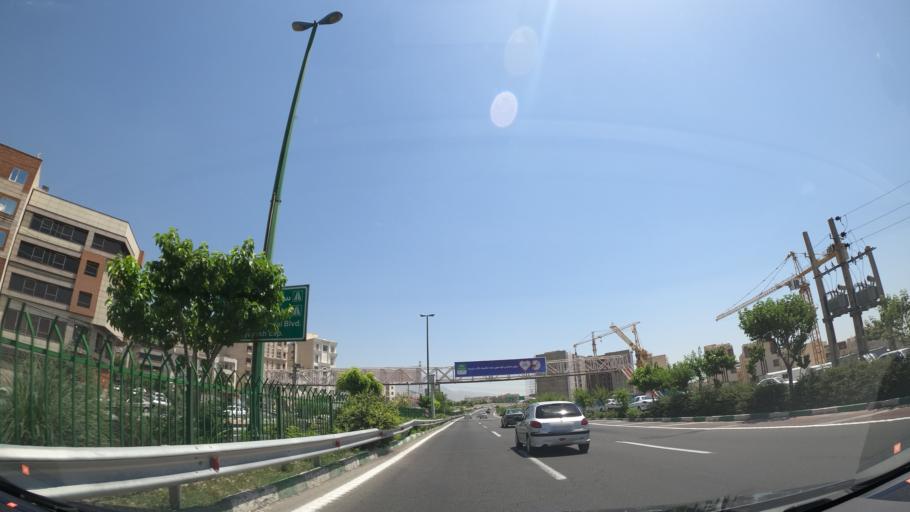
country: IR
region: Tehran
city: Tajrish
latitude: 35.7688
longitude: 51.3133
